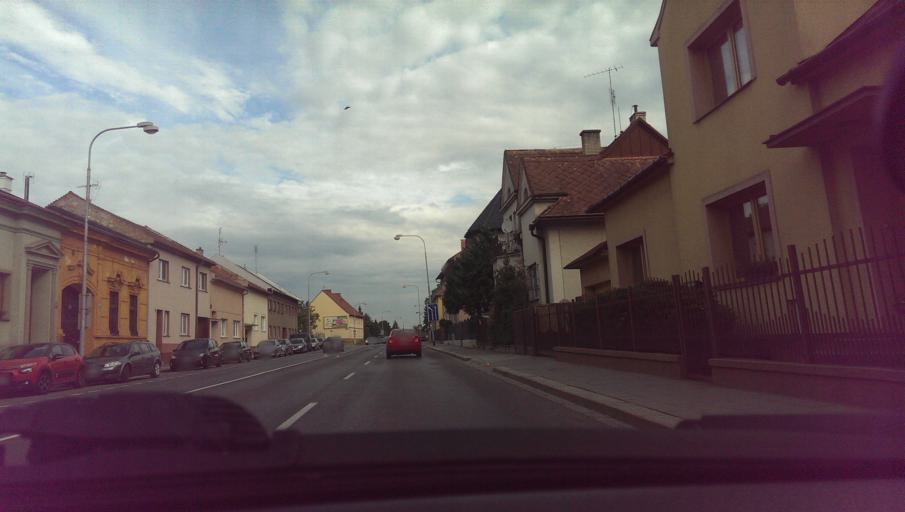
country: CZ
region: Zlin
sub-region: Okres Kromeriz
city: Kromeriz
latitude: 49.3022
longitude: 17.3844
